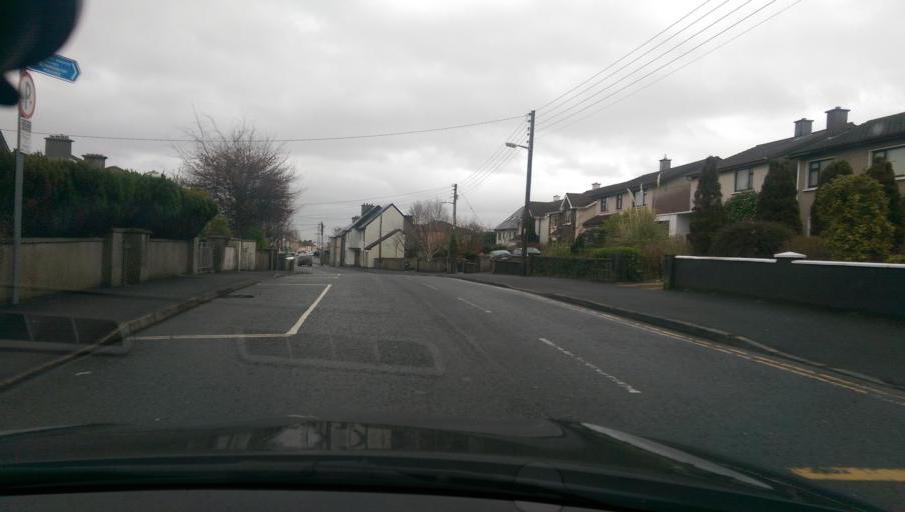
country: IE
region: Connaught
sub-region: County Galway
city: Gaillimh
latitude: 53.2729
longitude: -9.0703
